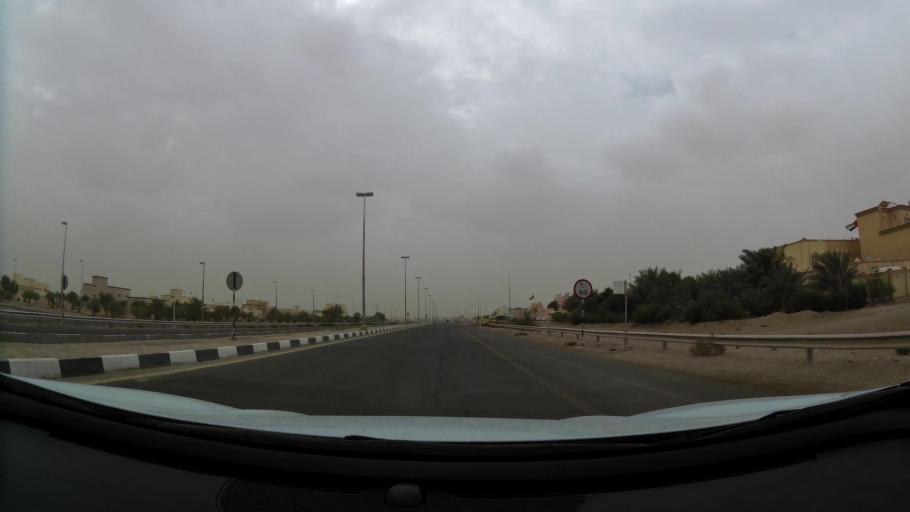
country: AE
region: Abu Dhabi
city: Abu Dhabi
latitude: 24.4244
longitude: 54.7427
